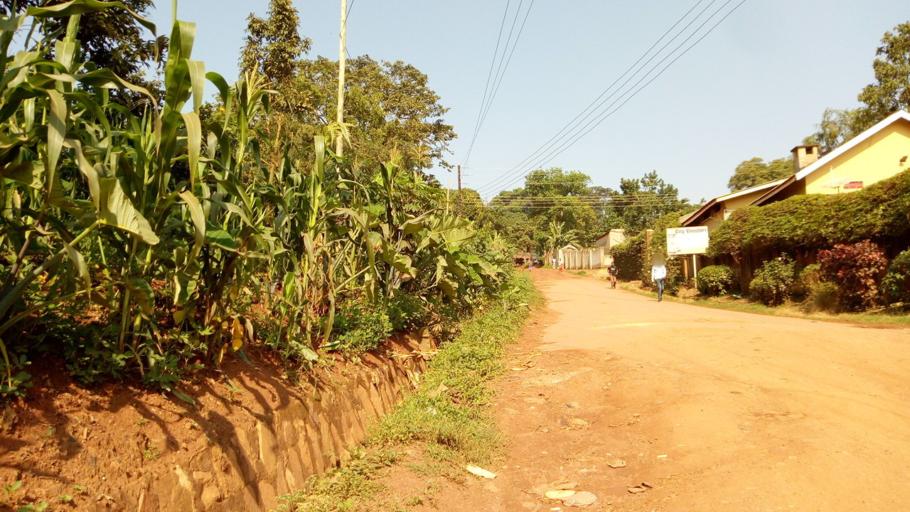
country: UG
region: Central Region
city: Kampala Central Division
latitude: 0.3414
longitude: 32.5668
